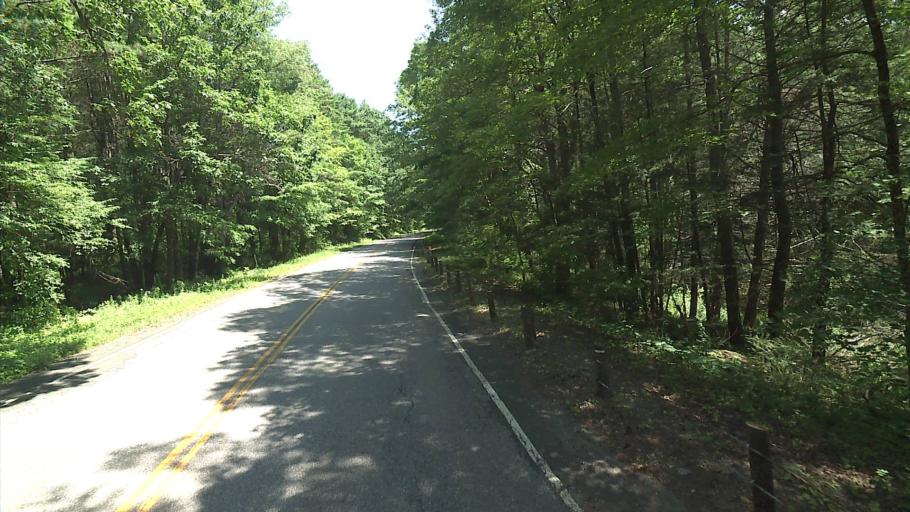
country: US
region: Connecticut
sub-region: Litchfield County
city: Canaan
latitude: 41.9091
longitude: -73.2779
